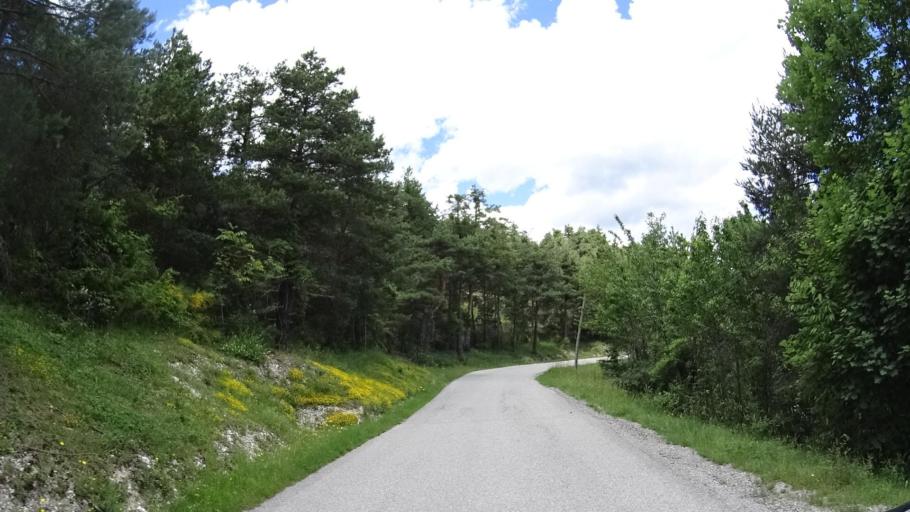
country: FR
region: Provence-Alpes-Cote d'Azur
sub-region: Departement des Alpes-de-Haute-Provence
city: Annot
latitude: 44.0150
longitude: 6.6271
